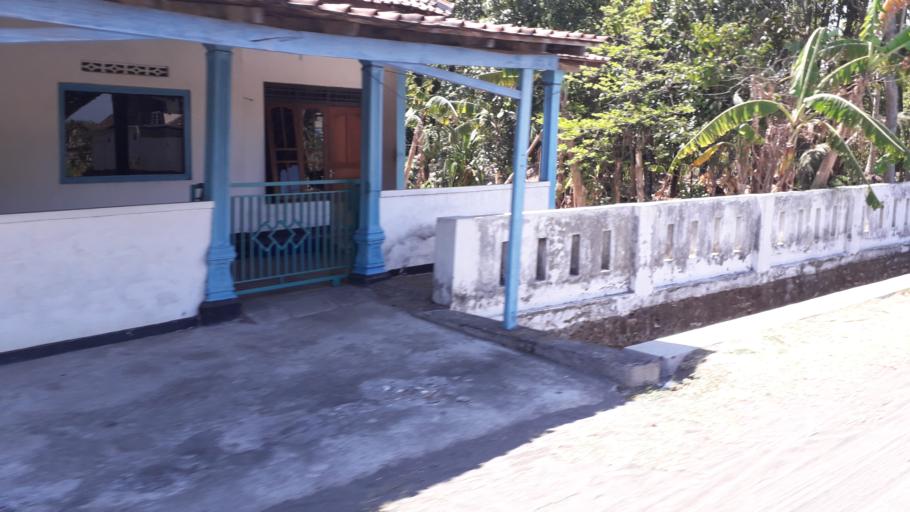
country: ID
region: Daerah Istimewa Yogyakarta
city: Pundong
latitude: -7.9847
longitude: 110.3159
